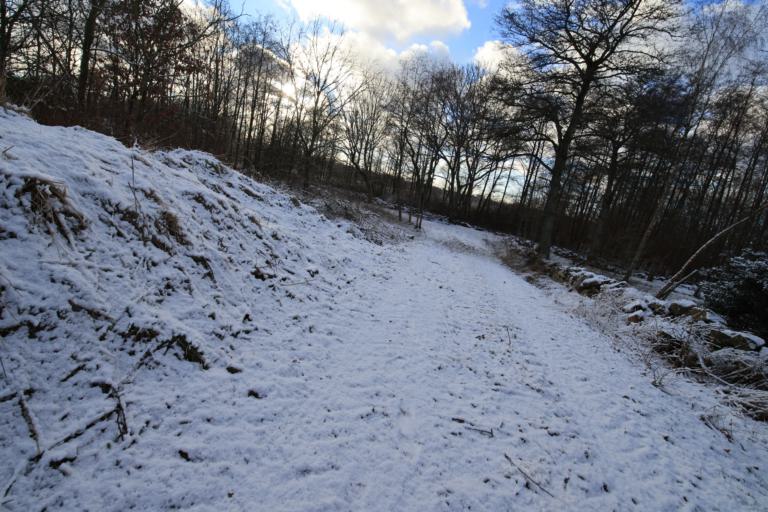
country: SE
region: Halland
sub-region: Varbergs Kommun
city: Varberg
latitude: 57.1329
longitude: 12.2935
